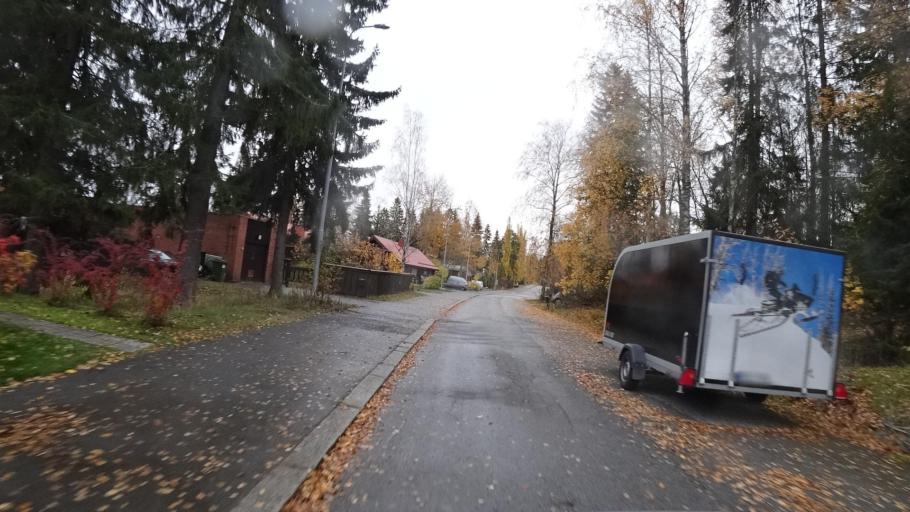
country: FI
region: Northern Savo
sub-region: Kuopio
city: Kuopio
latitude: 62.9291
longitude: 27.6928
